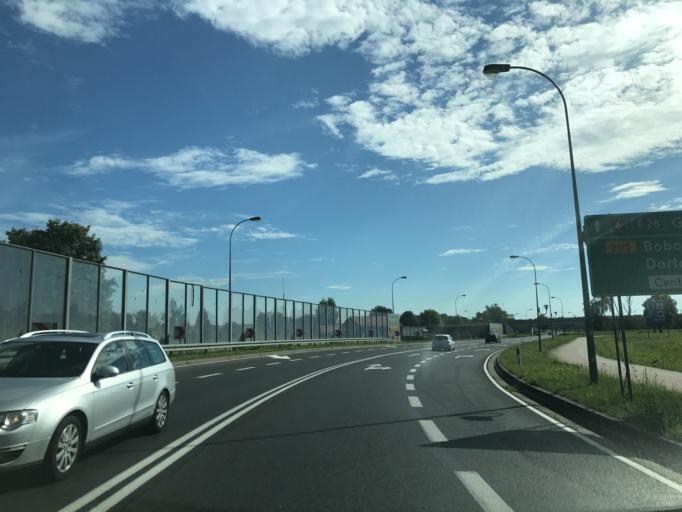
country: PL
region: West Pomeranian Voivodeship
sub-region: Powiat slawienski
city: Slawno
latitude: 54.3531
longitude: 16.6734
